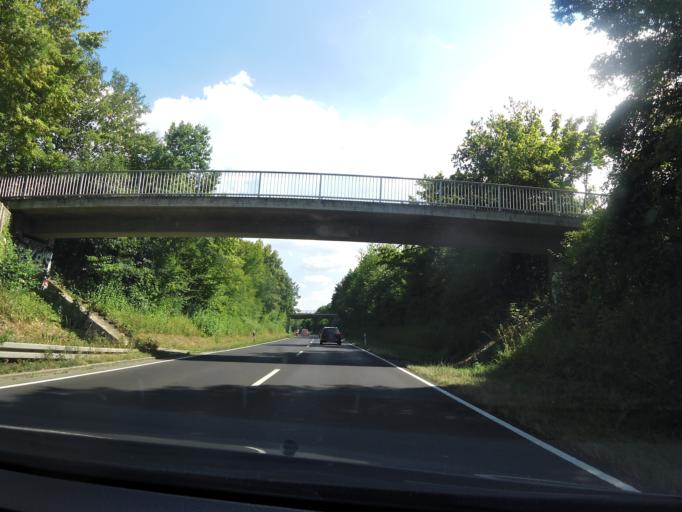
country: DE
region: Bavaria
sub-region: Regierungsbezirk Unterfranken
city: Margetshochheim
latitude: 49.8356
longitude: 9.8615
